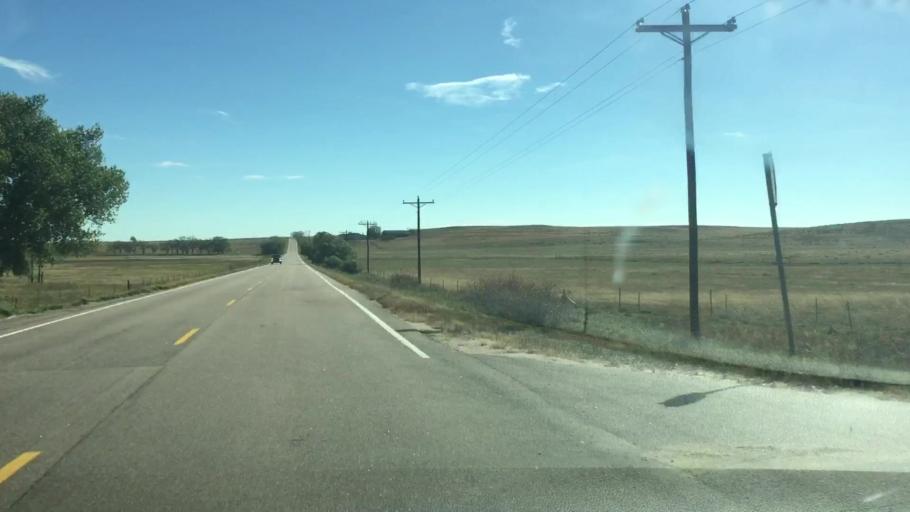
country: US
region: Colorado
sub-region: Elbert County
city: Kiowa
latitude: 39.2736
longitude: -104.1411
